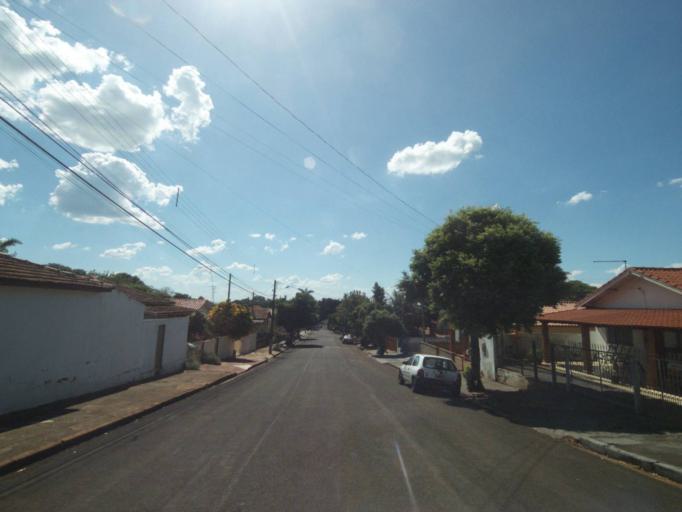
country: BR
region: Parana
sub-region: Sertanopolis
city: Sertanopolis
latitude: -23.0400
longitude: -50.8176
